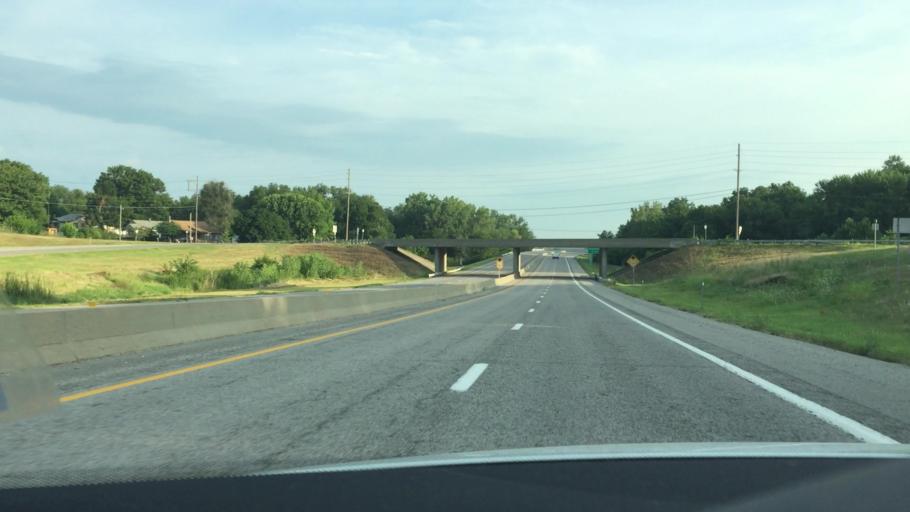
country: US
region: Kansas
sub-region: Doniphan County
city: Elwood
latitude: 39.7325
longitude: -94.8478
